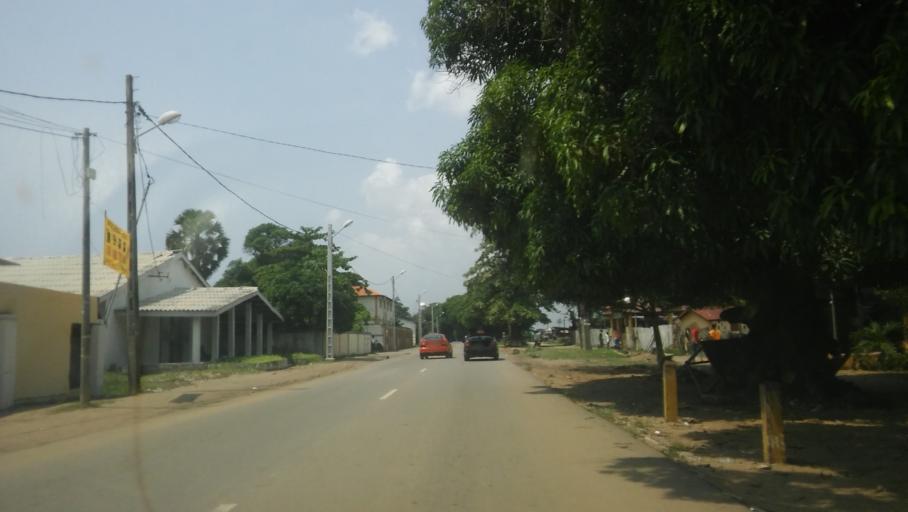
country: CI
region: Sud-Comoe
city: Grand-Bassam
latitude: 5.1969
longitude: -3.7340
